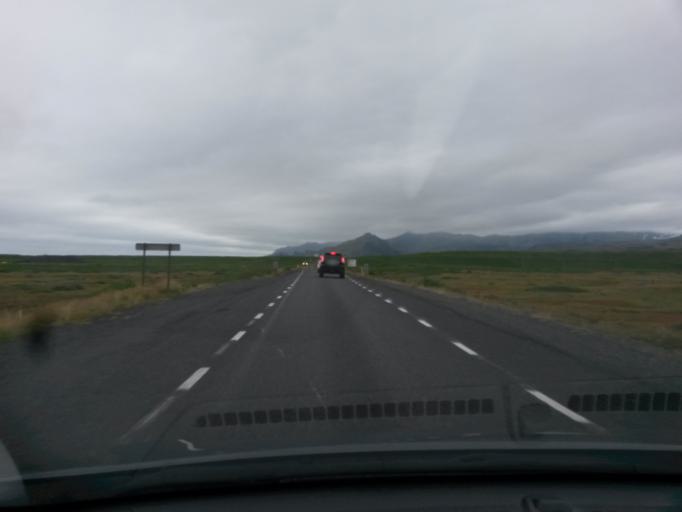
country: IS
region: South
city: Vestmannaeyjar
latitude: 63.4990
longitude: -19.4022
